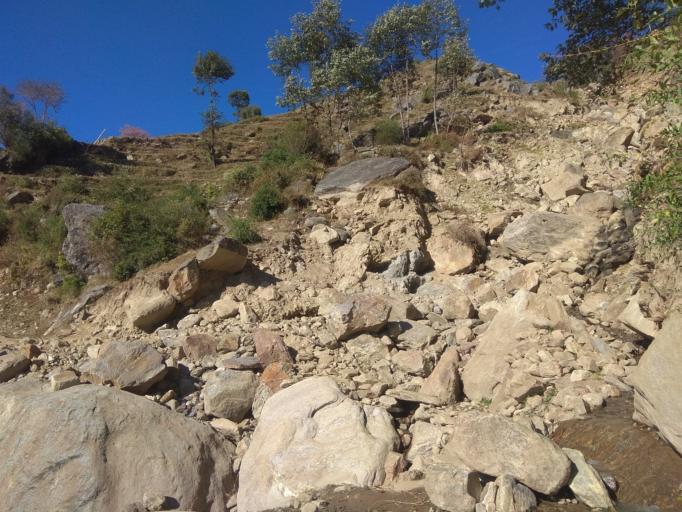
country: NP
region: Far Western
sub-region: Seti Zone
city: Achham
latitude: 29.2588
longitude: 81.6329
